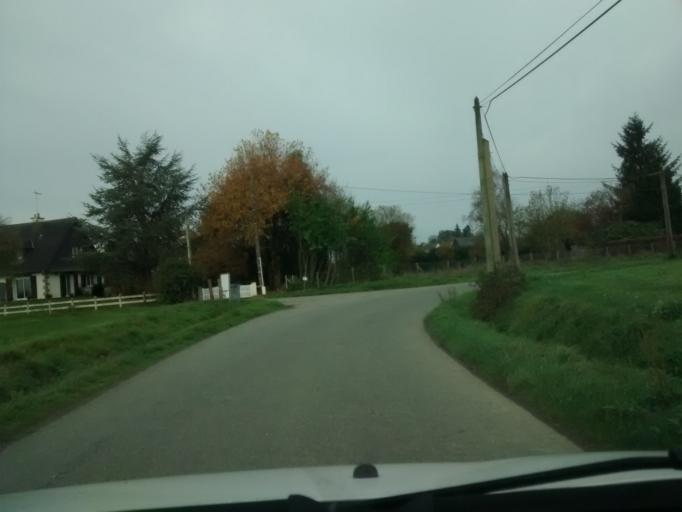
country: FR
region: Brittany
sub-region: Departement d'Ille-et-Vilaine
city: Noyal-sur-Vilaine
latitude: 48.1021
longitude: -1.5334
